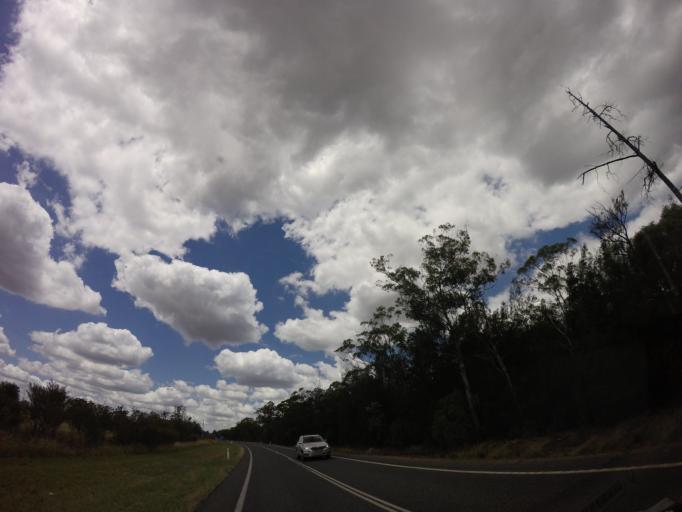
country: AU
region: Queensland
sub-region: Goondiwindi
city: Goondiwindi
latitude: -28.0071
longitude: 150.9247
